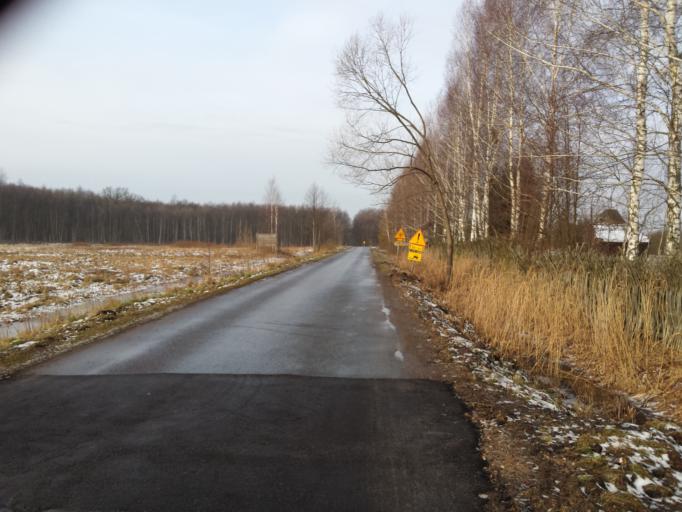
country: PL
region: Podlasie
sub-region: Powiat hajnowski
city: Bialowieza
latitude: 52.7013
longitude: 23.8349
